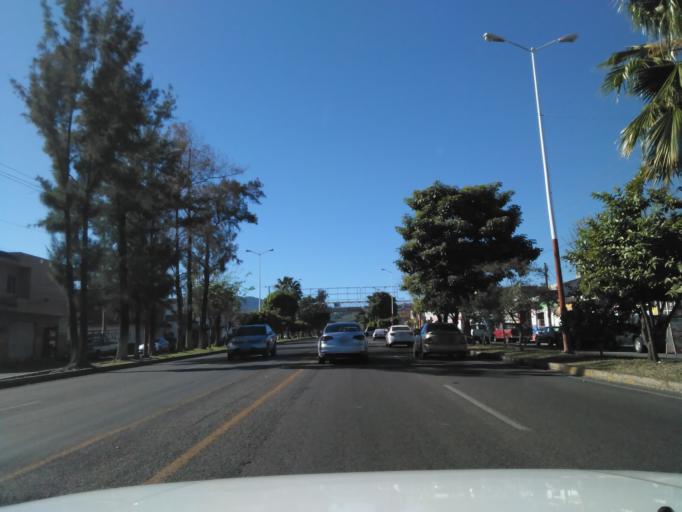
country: MX
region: Nayarit
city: Xalisco
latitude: 21.4550
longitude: -104.8964
